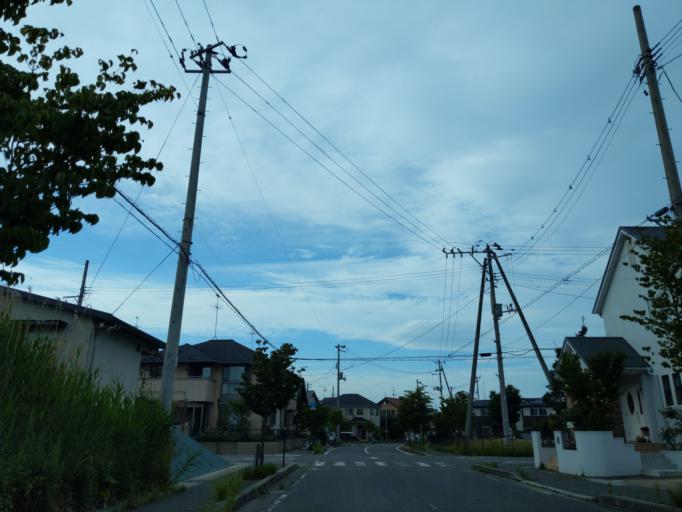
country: JP
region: Fukushima
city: Koriyama
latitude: 37.4214
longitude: 140.3634
